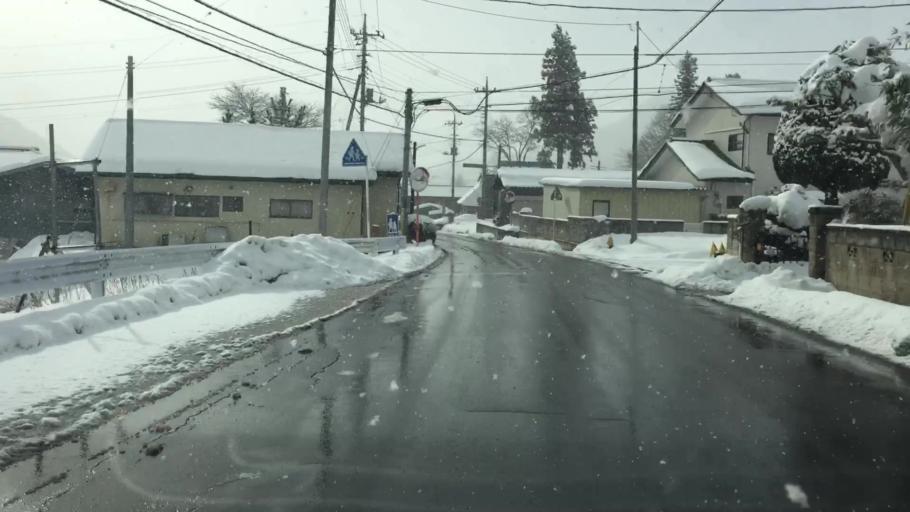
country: JP
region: Gunma
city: Numata
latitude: 36.6993
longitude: 139.0649
